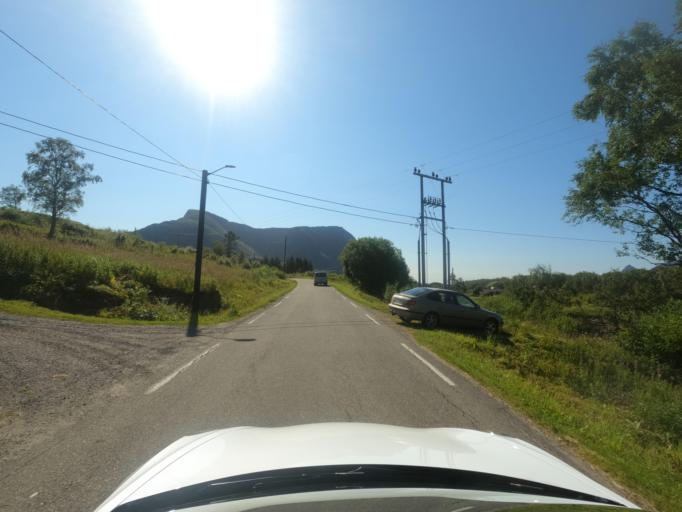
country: NO
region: Nordland
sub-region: Hadsel
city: Stokmarknes
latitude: 68.3063
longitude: 14.9972
